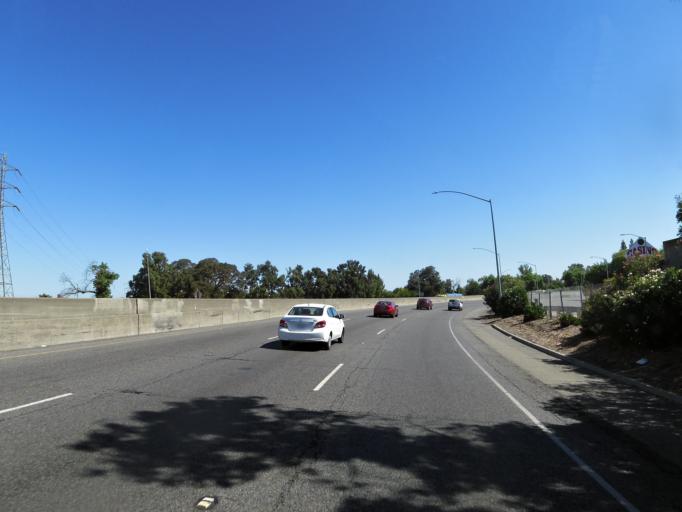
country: US
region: California
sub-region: Sacramento County
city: Arden-Arcade
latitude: 38.6221
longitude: -121.4192
